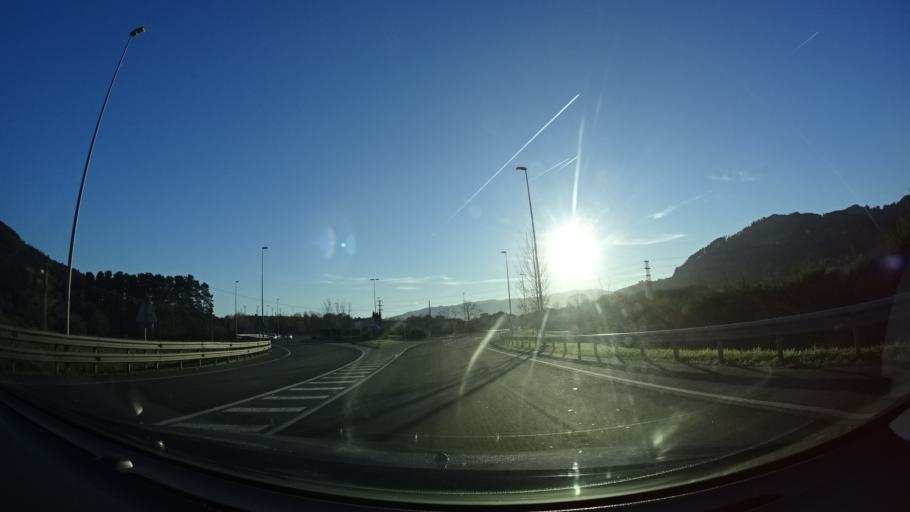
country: ES
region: Basque Country
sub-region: Bizkaia
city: Forua
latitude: 43.3235
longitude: -2.6684
